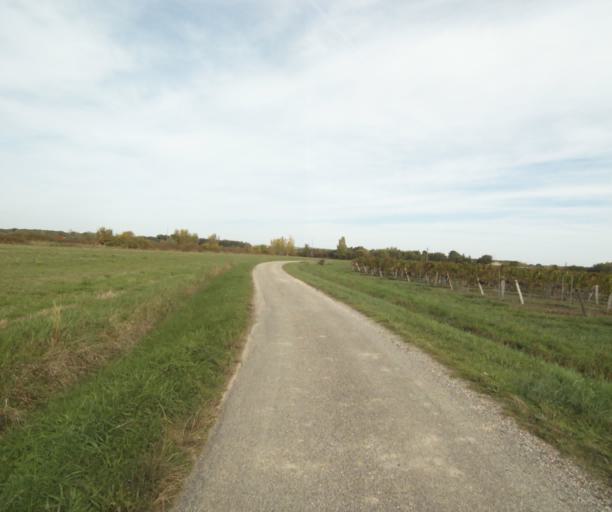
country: FR
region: Midi-Pyrenees
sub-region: Departement du Tarn-et-Garonne
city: Orgueil
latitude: 43.8909
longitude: 1.3959
